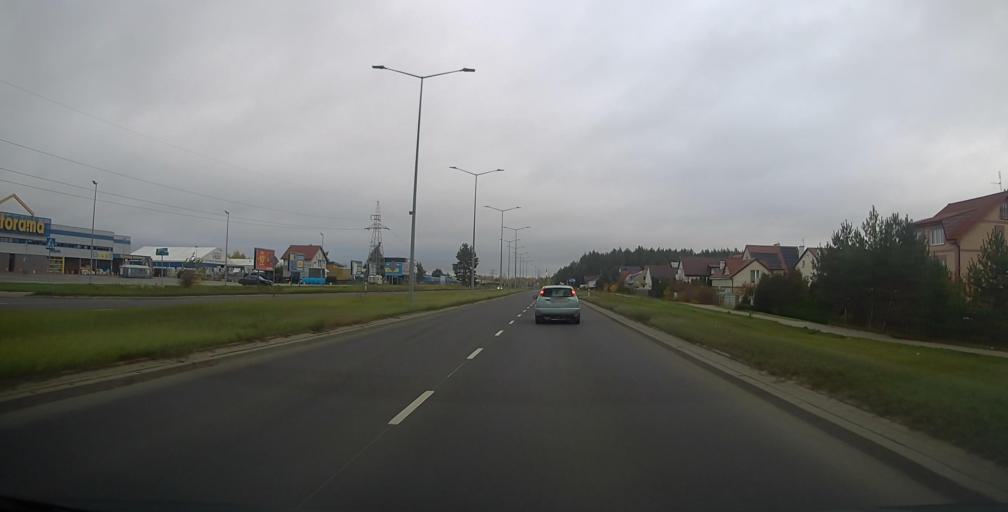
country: PL
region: Warmian-Masurian Voivodeship
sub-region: Powiat elcki
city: Elk
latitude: 53.8125
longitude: 22.3806
